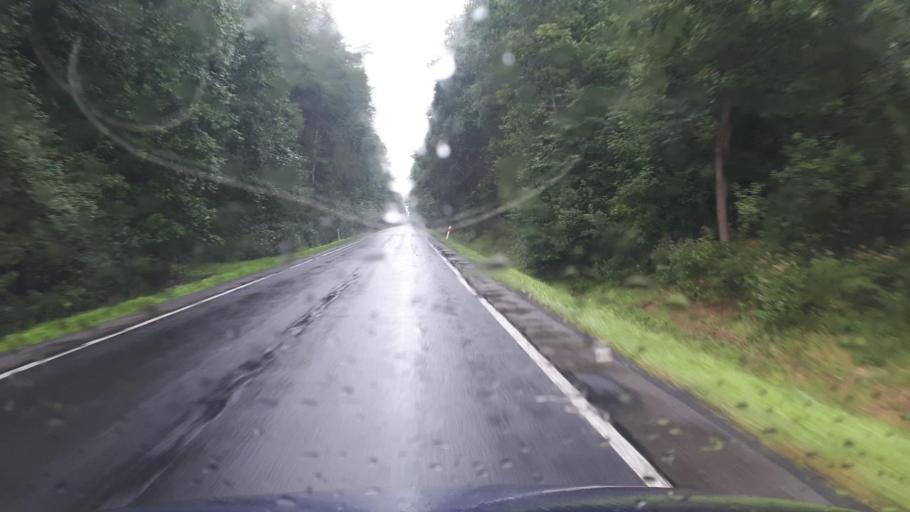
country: PL
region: Silesian Voivodeship
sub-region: Powiat tarnogorski
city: Tworog
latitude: 50.5309
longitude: 18.7009
